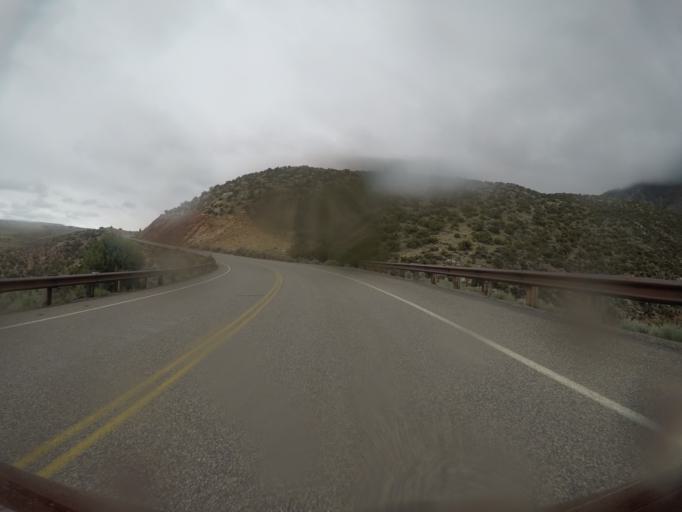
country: US
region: Wyoming
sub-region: Big Horn County
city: Lovell
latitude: 45.0464
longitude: -108.2538
